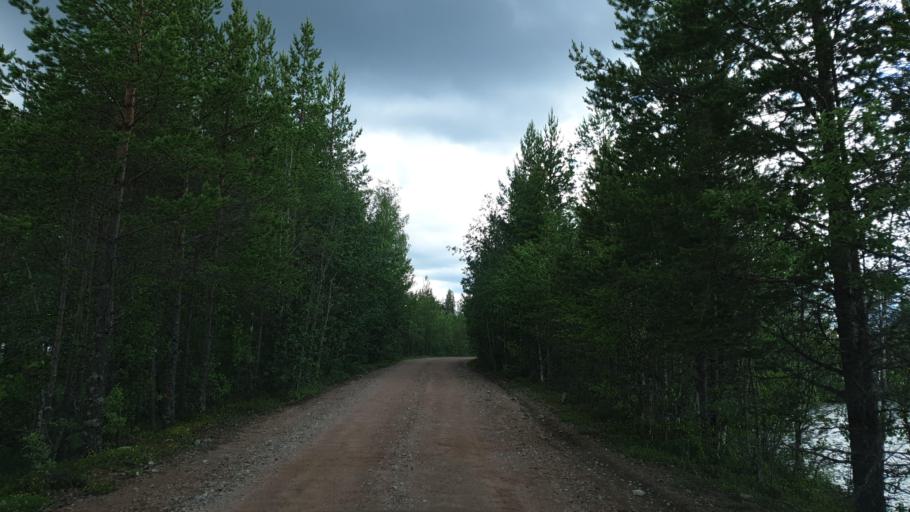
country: SE
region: Jaemtland
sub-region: Harjedalens Kommun
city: Sveg
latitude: 62.0341
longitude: 14.4926
